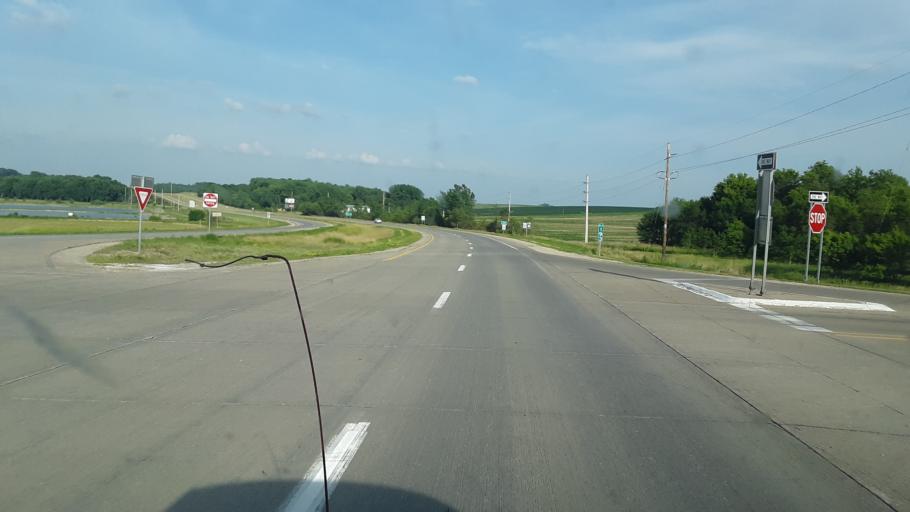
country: US
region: Iowa
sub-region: Marshall County
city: Marshalltown
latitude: 42.0074
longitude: -92.7676
